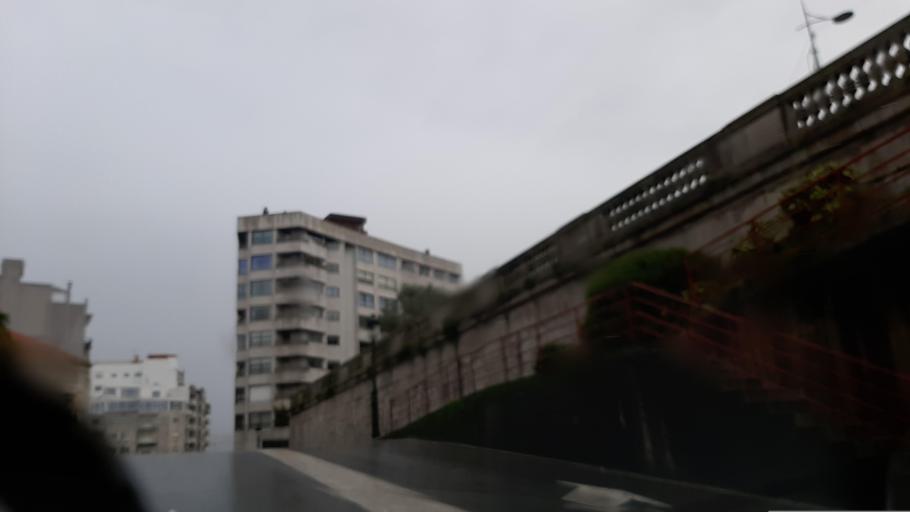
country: ES
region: Galicia
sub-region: Provincia de Pontevedra
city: Vigo
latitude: 42.2351
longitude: -8.7262
